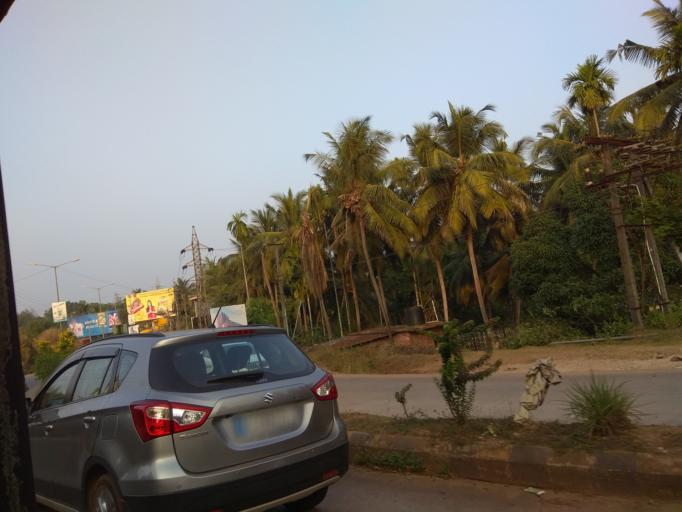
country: IN
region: Karnataka
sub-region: Dakshina Kannada
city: Mangalore
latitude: 12.9310
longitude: 74.8584
